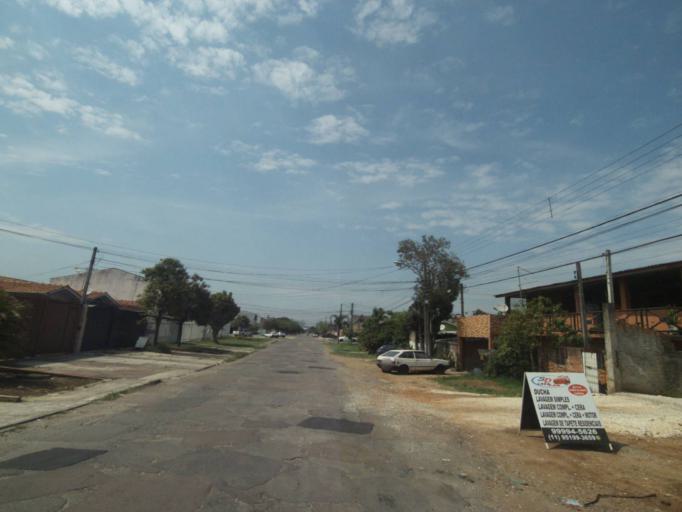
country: BR
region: Parana
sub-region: Pinhais
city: Pinhais
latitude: -25.4119
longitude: -49.2027
